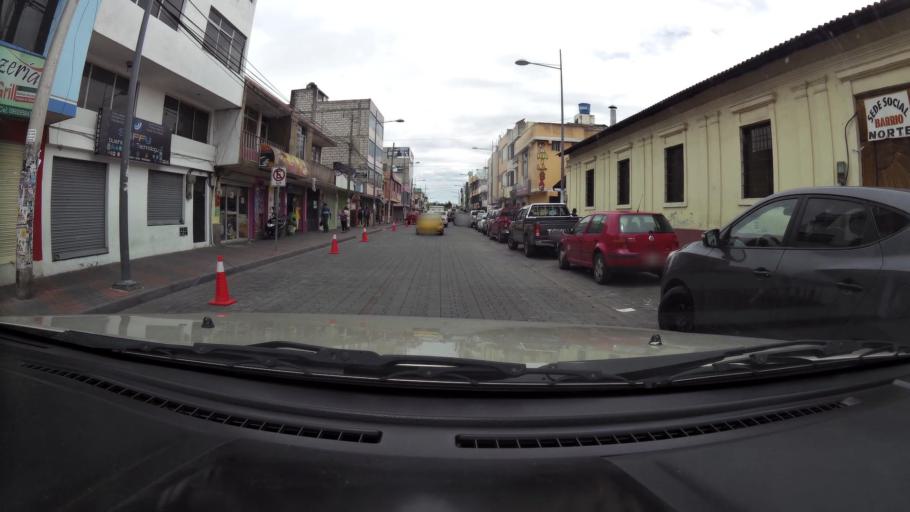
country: EC
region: Cotopaxi
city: San Miguel de Salcedo
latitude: -1.0184
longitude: -78.5921
